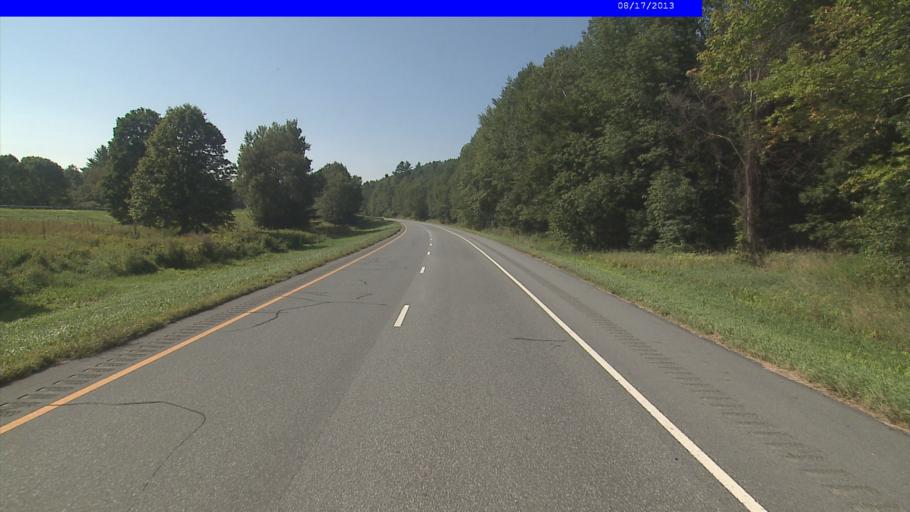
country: US
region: Vermont
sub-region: Windsor County
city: Windsor
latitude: 43.5739
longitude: -72.3863
